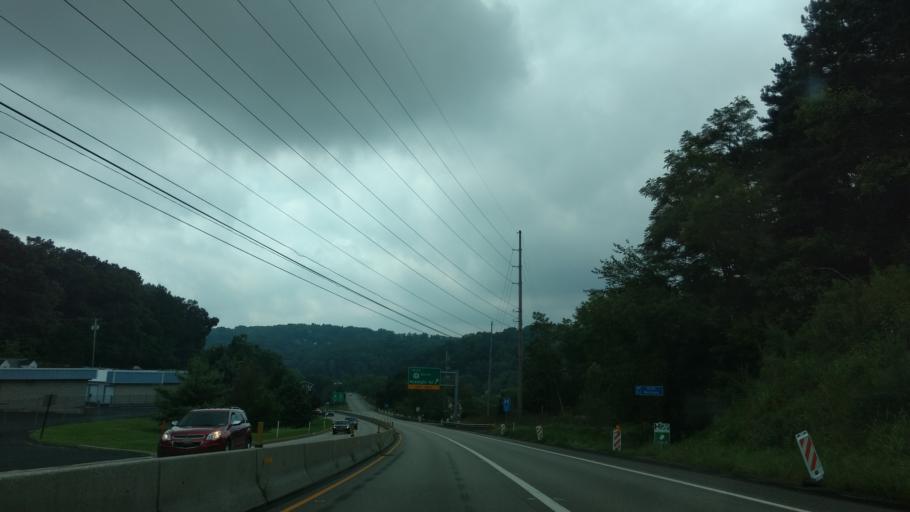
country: US
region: Pennsylvania
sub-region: Allegheny County
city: Franklin Park
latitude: 40.5929
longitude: -80.0478
